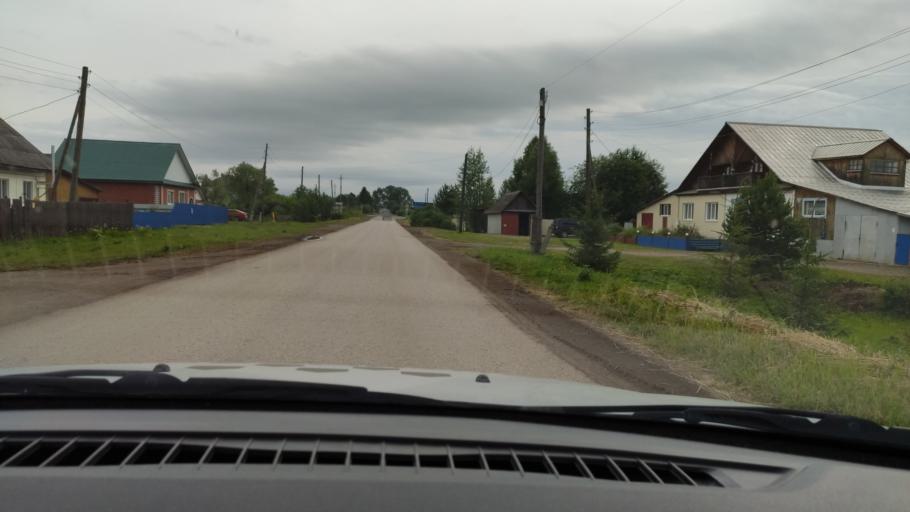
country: RU
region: Perm
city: Orda
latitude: 57.2943
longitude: 56.6488
